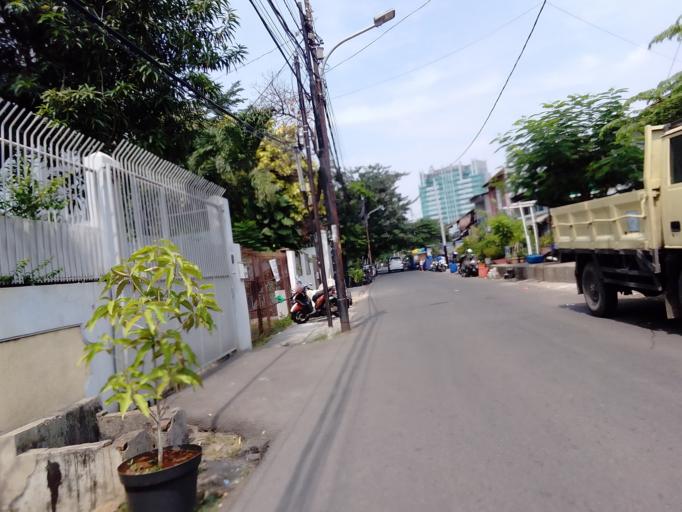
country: ID
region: Jakarta Raya
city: Jakarta
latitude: -6.1777
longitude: 106.8091
